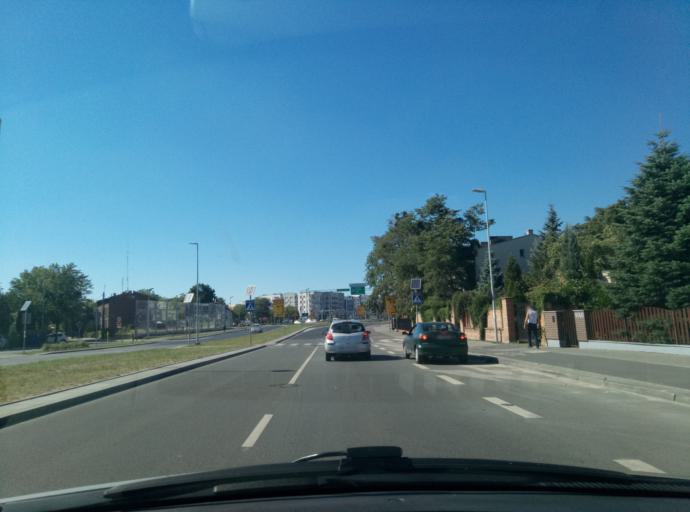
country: PL
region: Kujawsko-Pomorskie
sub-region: Torun
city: Torun
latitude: 53.0235
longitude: 18.5939
